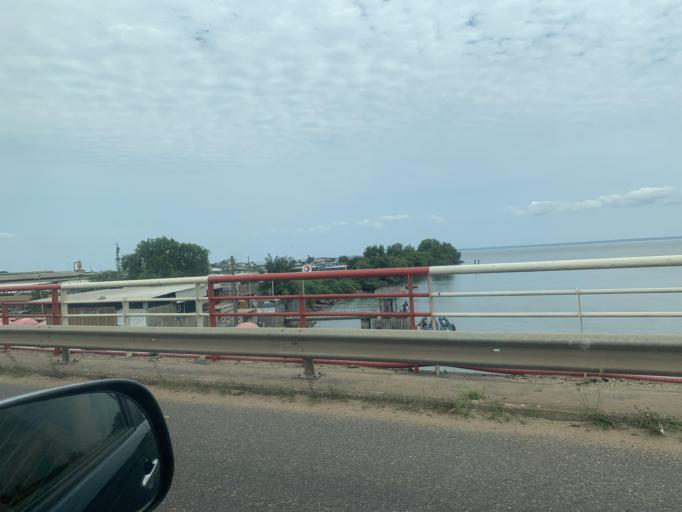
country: GA
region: Estuaire
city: Libreville
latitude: 0.3426
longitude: 9.4760
